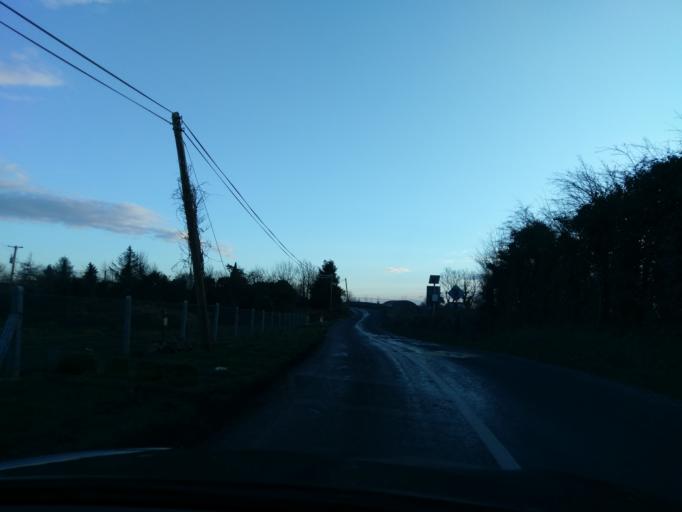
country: IE
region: Connaught
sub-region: County Galway
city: Loughrea
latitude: 53.3222
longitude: -8.6083
